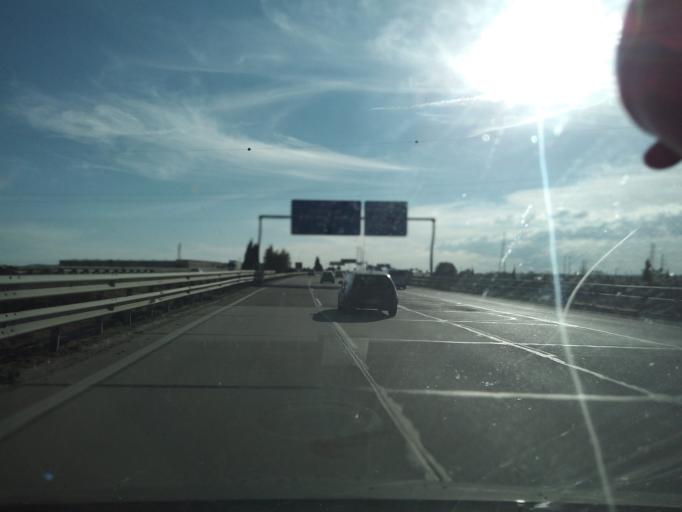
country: ES
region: Madrid
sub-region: Provincia de Madrid
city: Pinto
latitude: 40.2738
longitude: -3.6993
